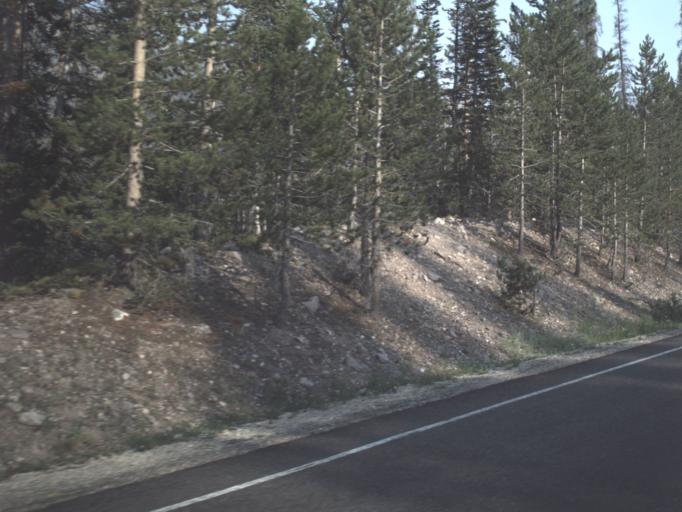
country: US
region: Utah
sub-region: Summit County
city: Kamas
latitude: 40.7613
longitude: -110.8822
